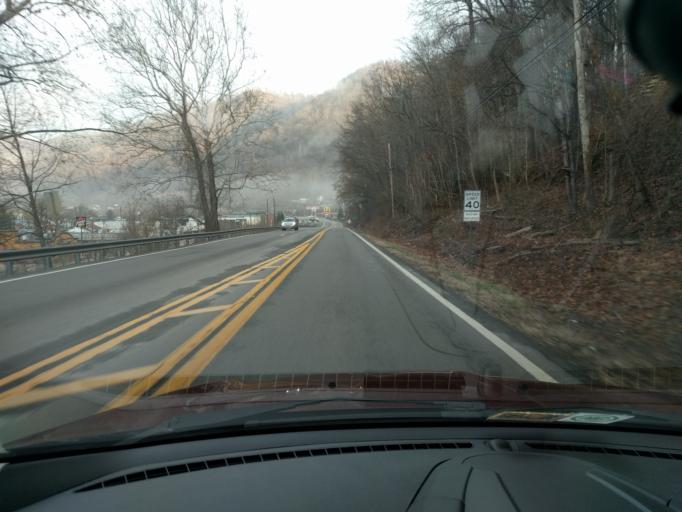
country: US
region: West Virginia
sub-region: Kanawha County
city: Montgomery
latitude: 38.1782
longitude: -81.3048
